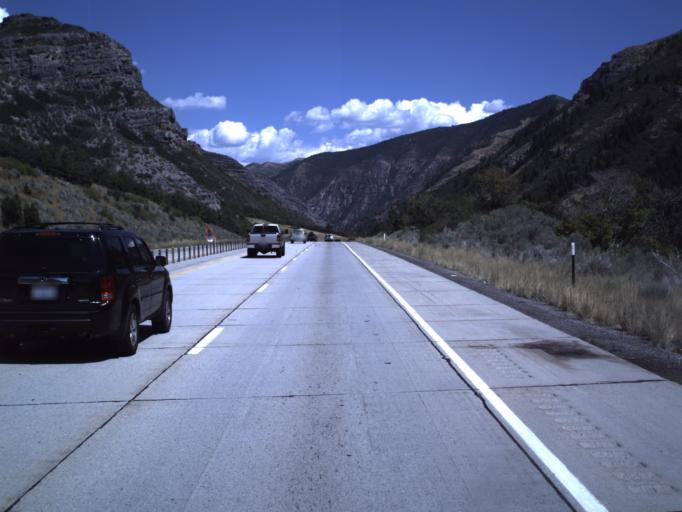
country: US
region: Utah
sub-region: Utah County
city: Orem
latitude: 40.3463
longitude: -111.5977
